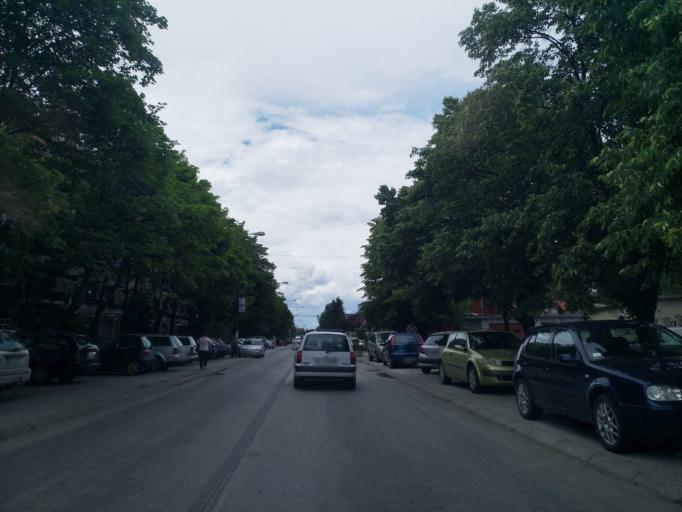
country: RS
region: Central Serbia
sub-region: Pomoravski Okrug
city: Jagodina
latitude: 43.9693
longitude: 21.2754
